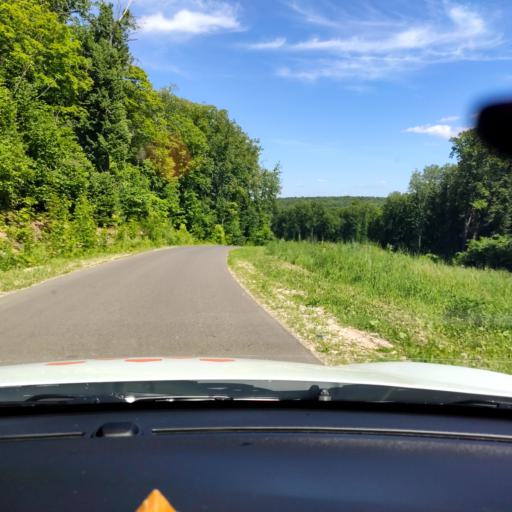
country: RU
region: Tatarstan
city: Sviyazhsk
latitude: 55.7757
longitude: 48.7808
